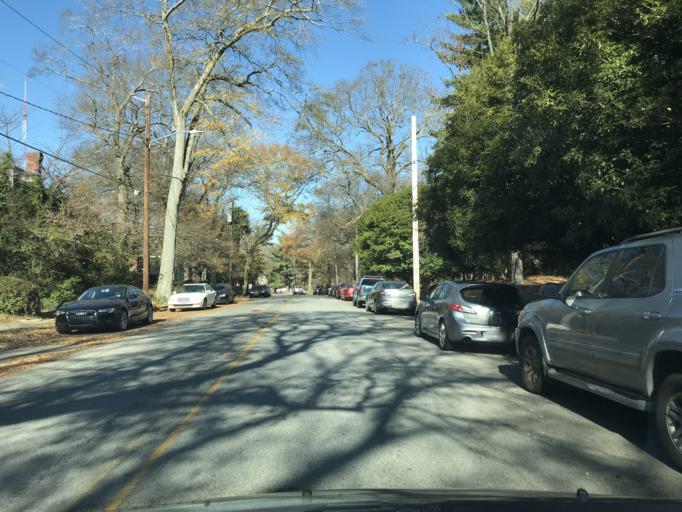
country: US
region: Georgia
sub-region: DeKalb County
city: Druid Hills
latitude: 33.7580
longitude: -84.3543
